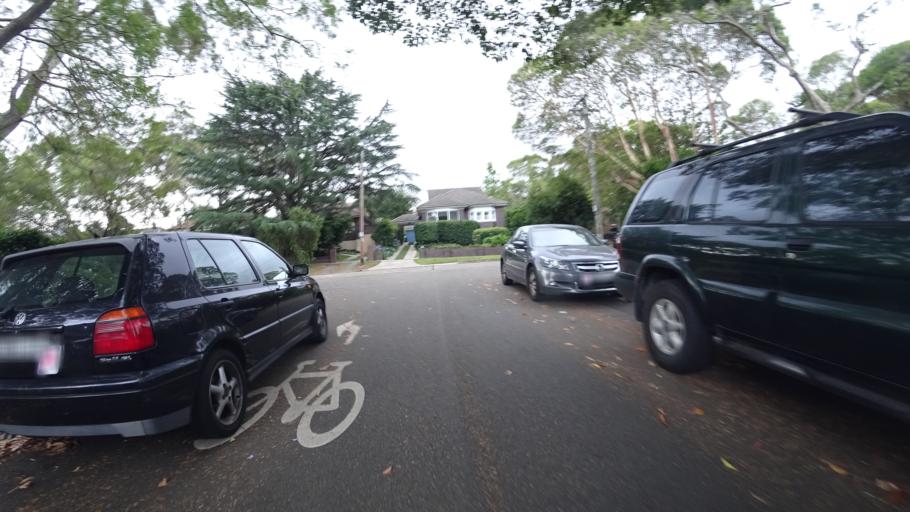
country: AU
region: New South Wales
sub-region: Willoughby
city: Chatswood
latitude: -33.8049
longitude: 151.1885
